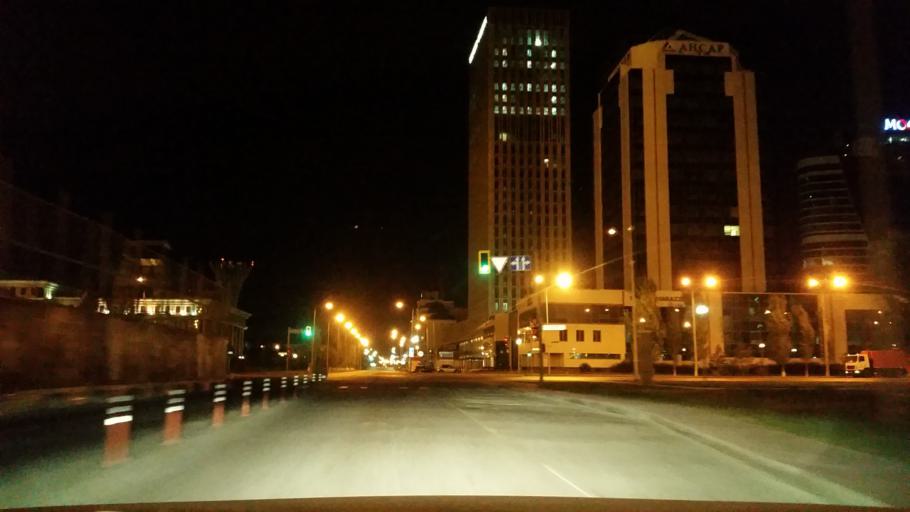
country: KZ
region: Astana Qalasy
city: Astana
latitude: 51.1223
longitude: 71.4301
